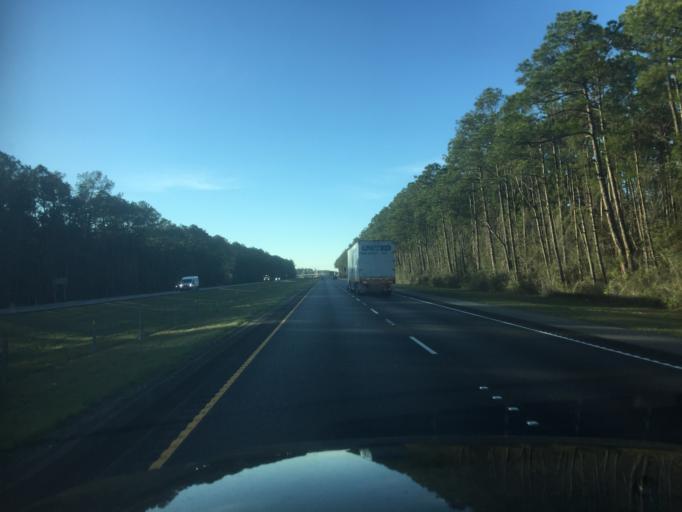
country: US
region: Louisiana
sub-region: Saint Tammany Parish
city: Mandeville
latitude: 30.3867
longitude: -89.9898
